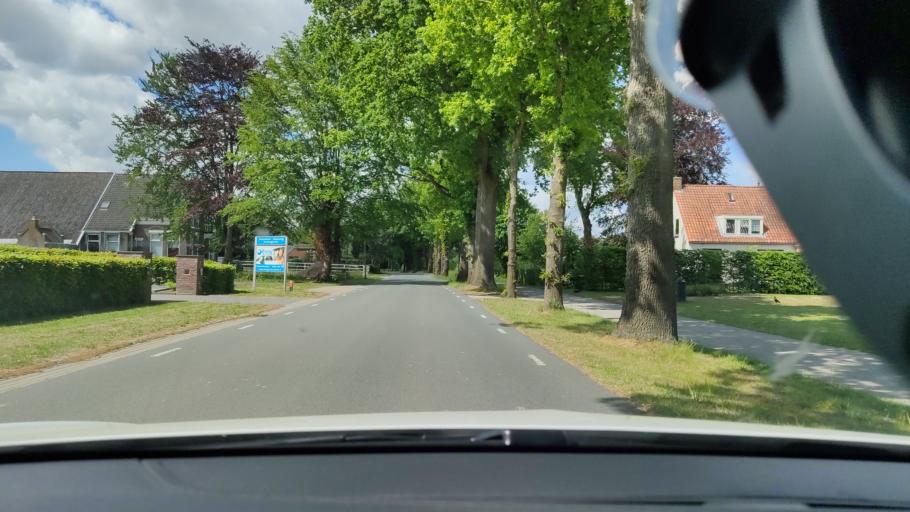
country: NL
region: Drenthe
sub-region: Gemeente Tynaarlo
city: Zuidlaren
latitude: 53.1014
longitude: 6.6882
